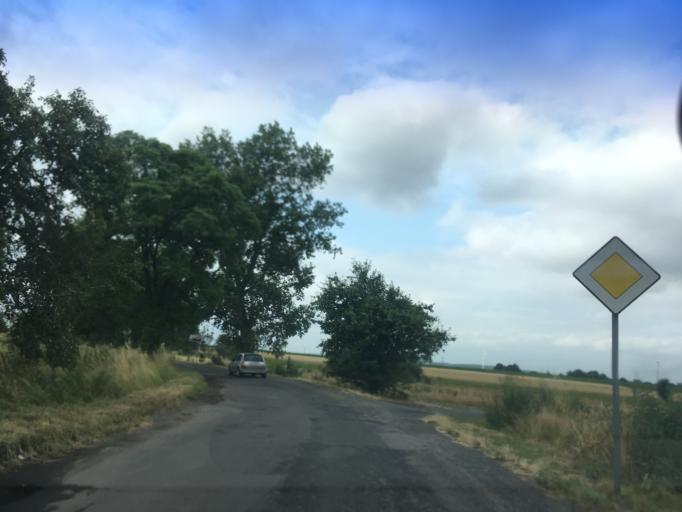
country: PL
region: Lower Silesian Voivodeship
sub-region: Powiat zgorzelecki
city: Sulikow
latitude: 51.1012
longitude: 15.0652
